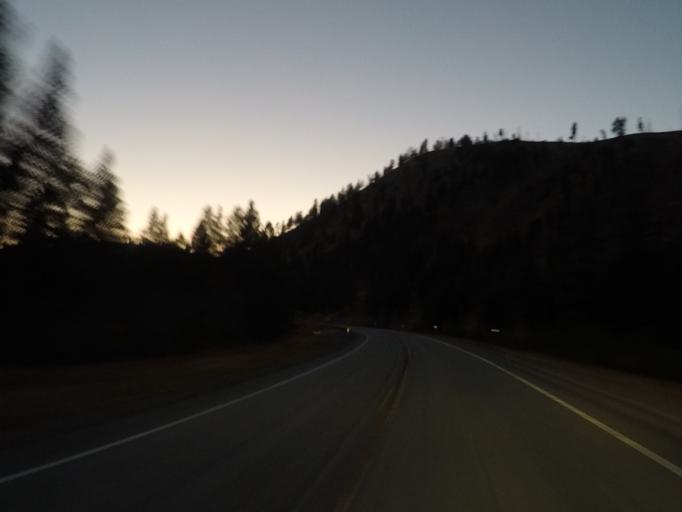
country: US
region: Montana
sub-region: Missoula County
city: Seeley Lake
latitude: 47.0249
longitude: -113.3059
